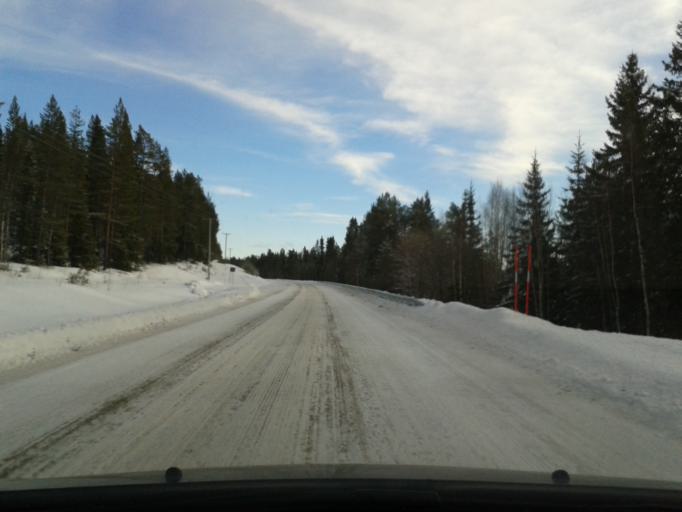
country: SE
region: Vaesterbotten
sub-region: Vilhelmina Kommun
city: Vilhelmina
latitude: 64.3705
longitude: 16.9151
